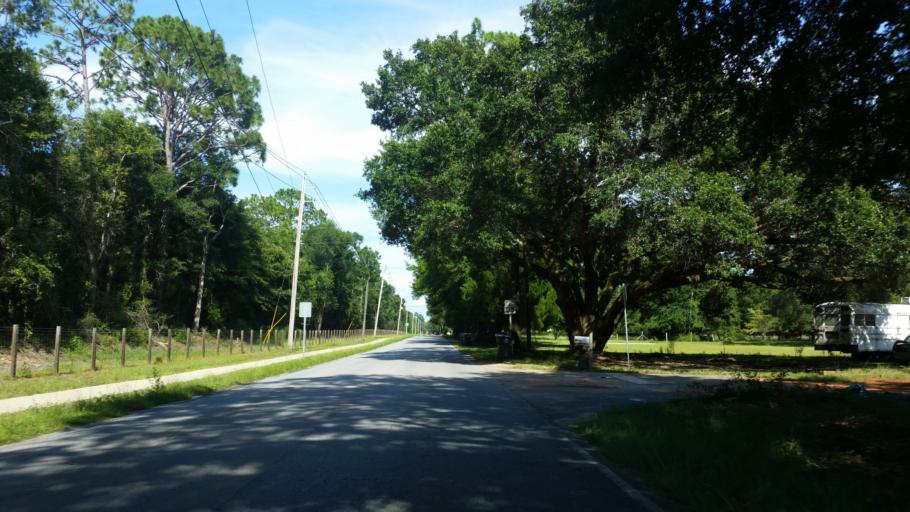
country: US
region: Florida
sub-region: Santa Rosa County
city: Pace
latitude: 30.6182
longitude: -87.1400
